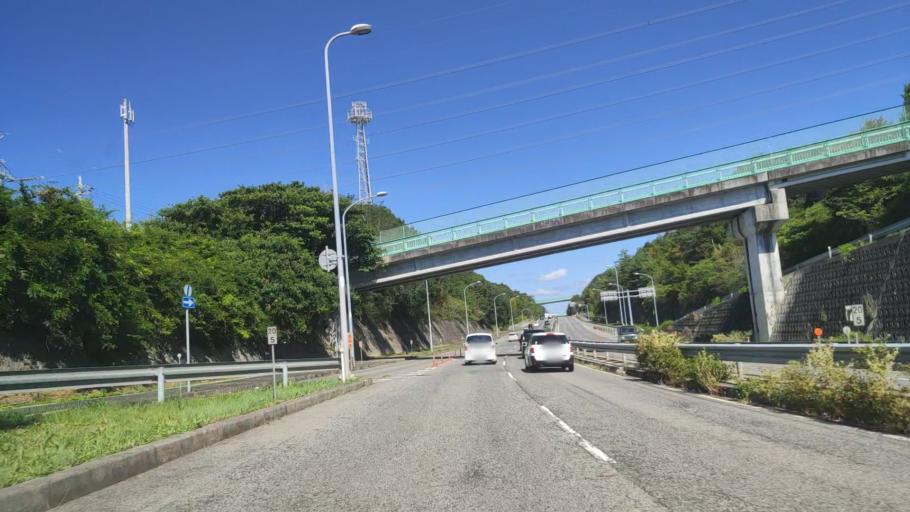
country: JP
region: Hyogo
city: Ono
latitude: 34.8220
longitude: 134.9508
